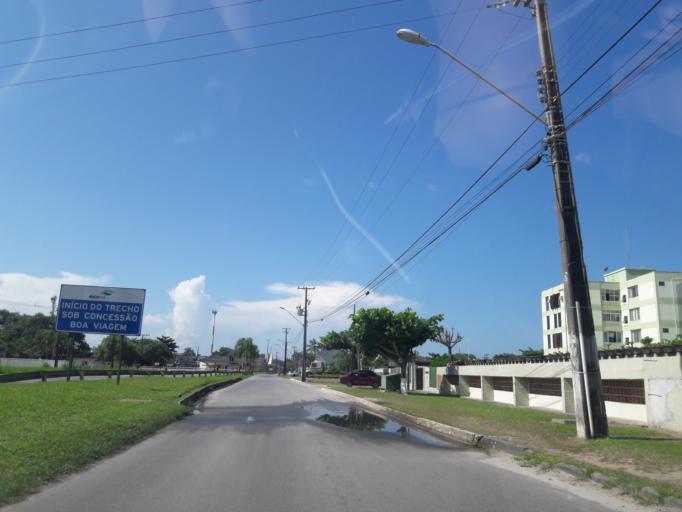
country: BR
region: Parana
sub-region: Pontal Do Parana
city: Pontal do Parana
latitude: -25.7017
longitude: -48.4740
